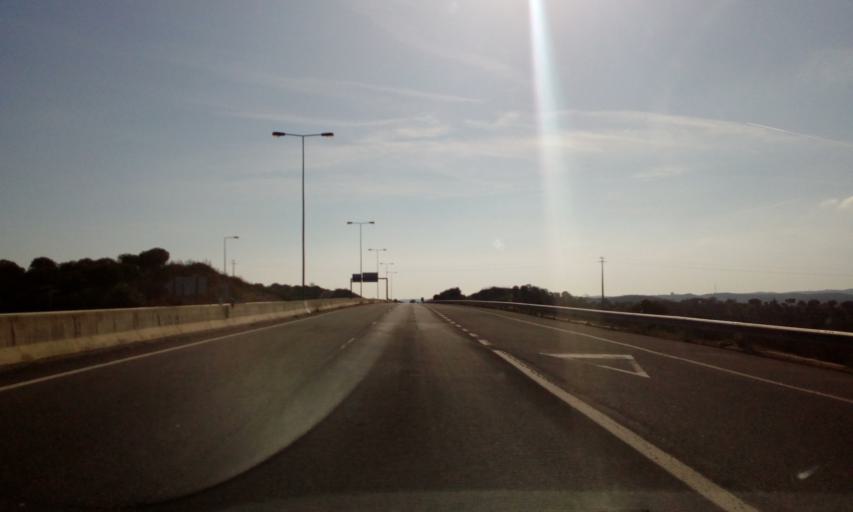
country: PT
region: Faro
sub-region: Castro Marim
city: Castro Marim
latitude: 37.2924
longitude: -7.4873
